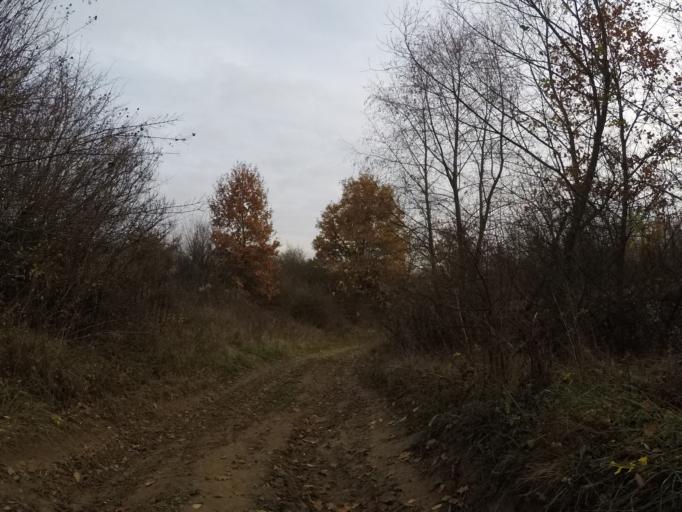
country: SK
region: Presovsky
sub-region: Okres Presov
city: Presov
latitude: 48.9396
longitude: 21.1739
